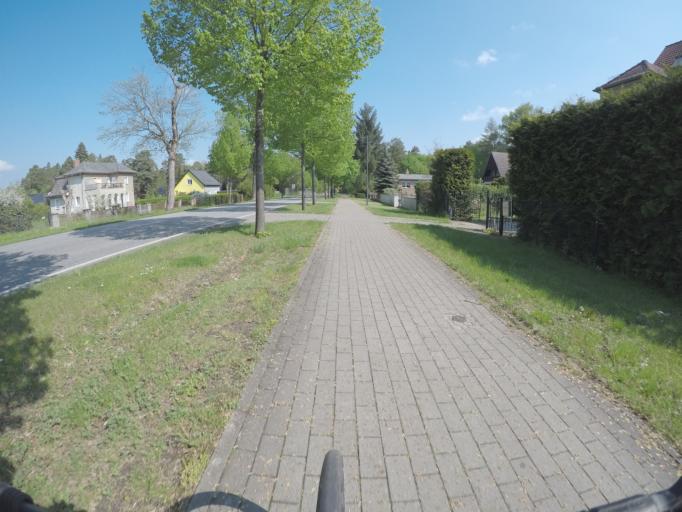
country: DE
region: Brandenburg
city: Wandlitz
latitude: 52.7645
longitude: 13.4746
